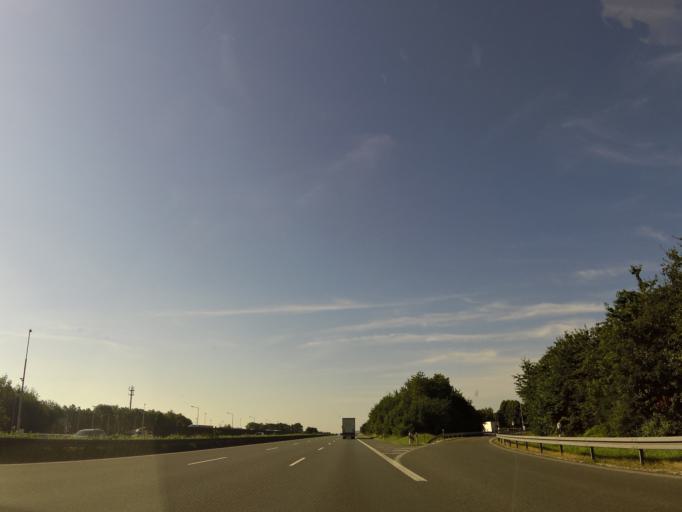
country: DE
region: Bavaria
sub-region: Regierungsbezirk Mittelfranken
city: Allersberg
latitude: 49.2237
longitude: 11.2243
